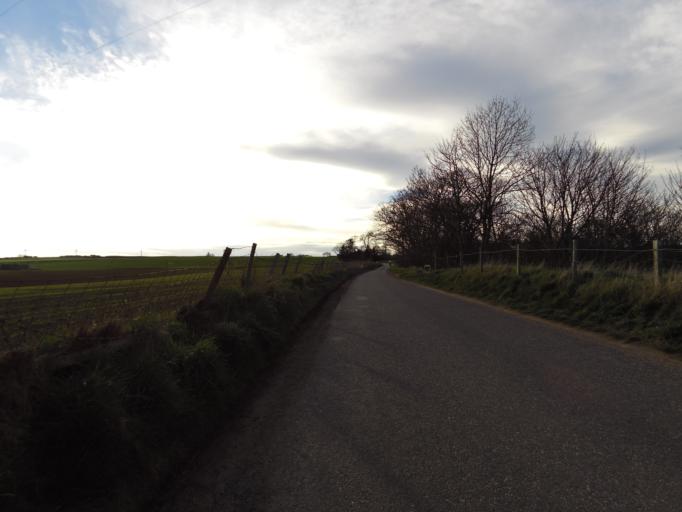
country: GB
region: Scotland
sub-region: Aberdeenshire
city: Stonehaven
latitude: 56.8980
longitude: -2.2199
